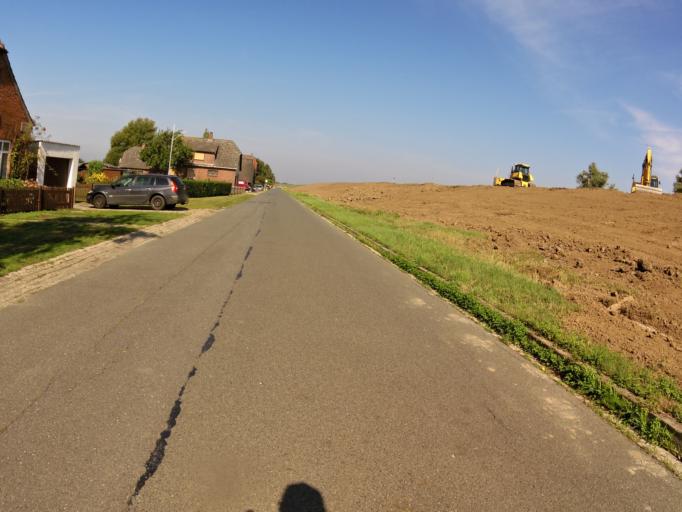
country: DE
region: Lower Saxony
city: Neuenkirchen
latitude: 53.2007
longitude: 8.4965
